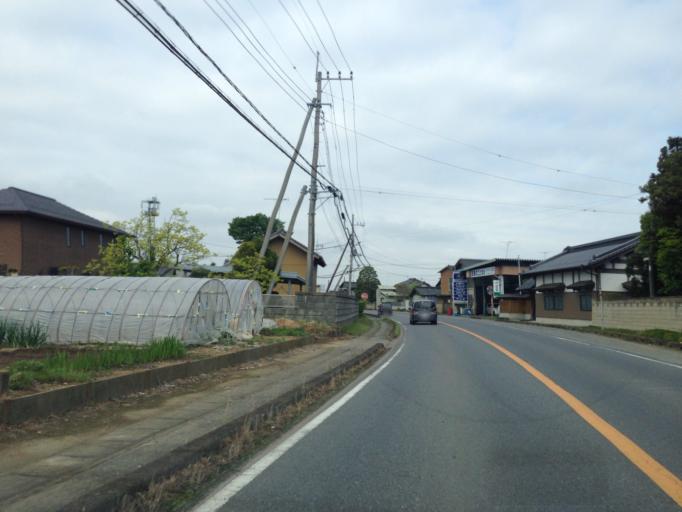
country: JP
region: Ibaraki
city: Ishige
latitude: 36.1524
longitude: 139.9857
